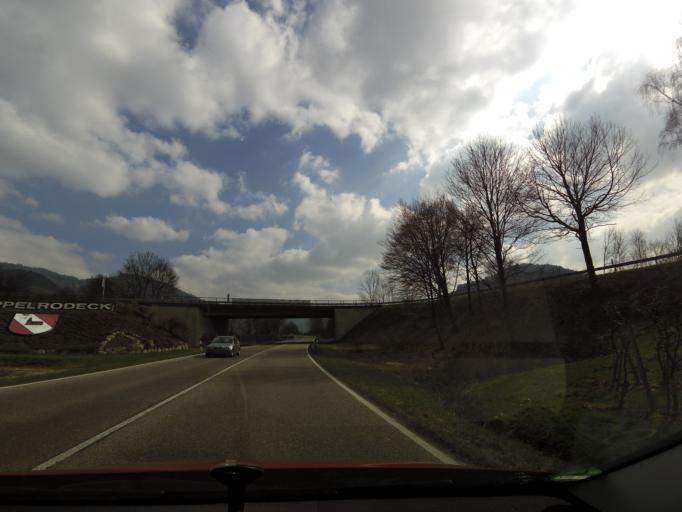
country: DE
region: Baden-Wuerttemberg
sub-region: Freiburg Region
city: Kappelrodeck
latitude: 48.5956
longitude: 8.1095
